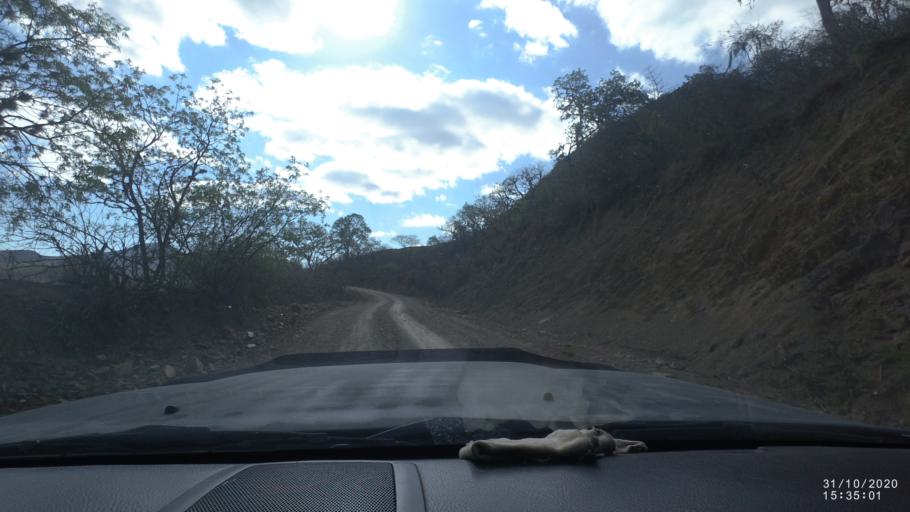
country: BO
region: Chuquisaca
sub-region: Provincia Zudanez
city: Mojocoya
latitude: -18.3412
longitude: -64.7522
